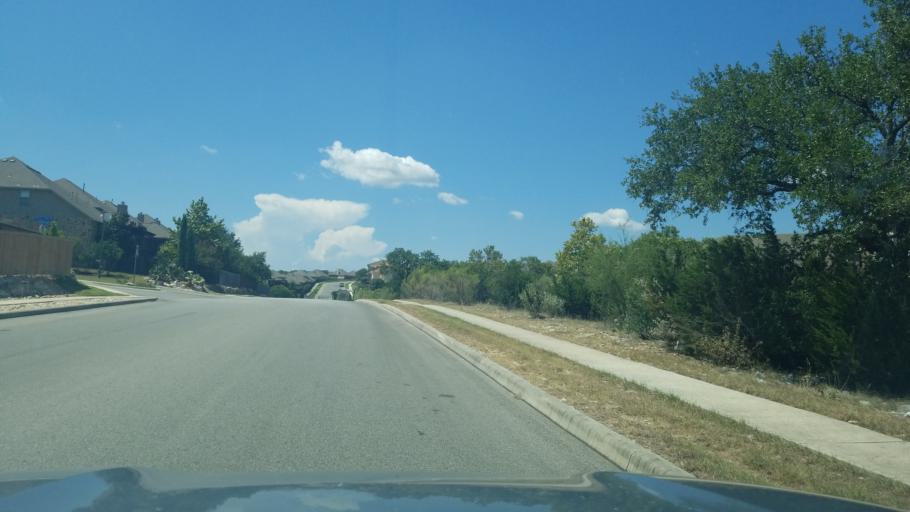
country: US
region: Texas
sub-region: Bexar County
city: Timberwood Park
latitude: 29.6685
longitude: -98.4864
